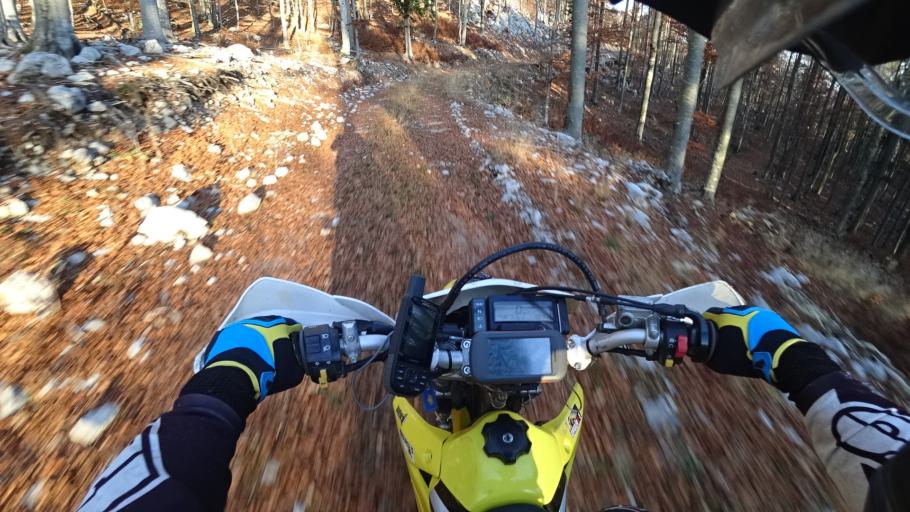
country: HR
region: Primorsko-Goranska
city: Drazice
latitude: 45.4826
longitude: 14.4869
